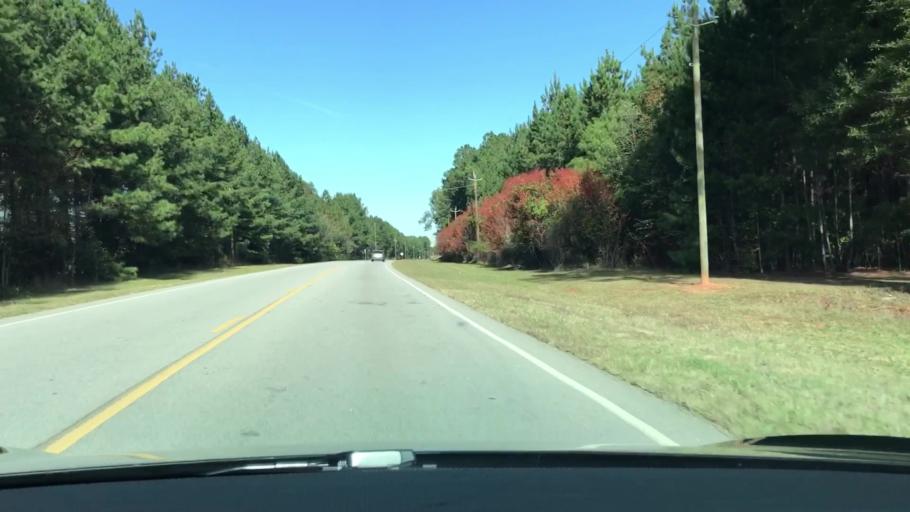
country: US
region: Georgia
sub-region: Warren County
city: Firing Range
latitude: 33.4384
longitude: -82.6905
